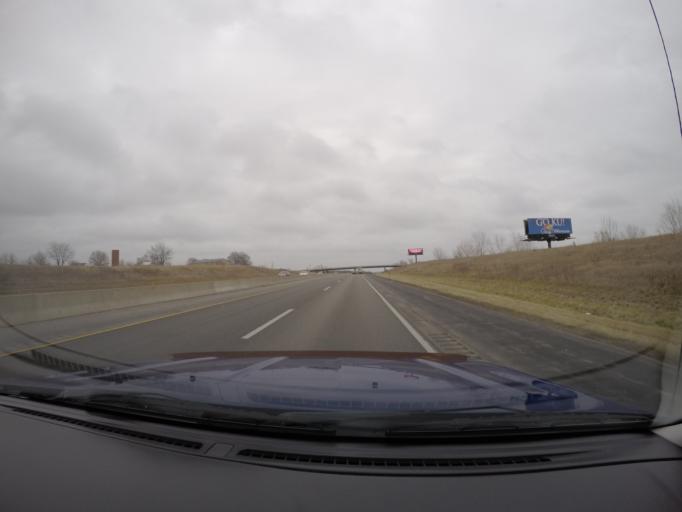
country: US
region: Kansas
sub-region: Leavenworth County
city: Basehor
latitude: 39.0824
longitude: -94.9492
